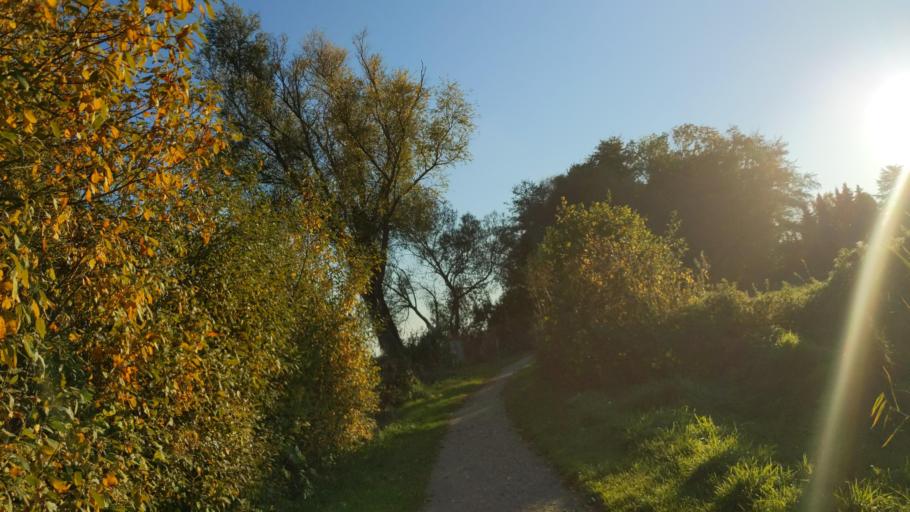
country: DE
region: Schleswig-Holstein
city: Gross Sarau
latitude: 53.7695
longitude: 10.7400
